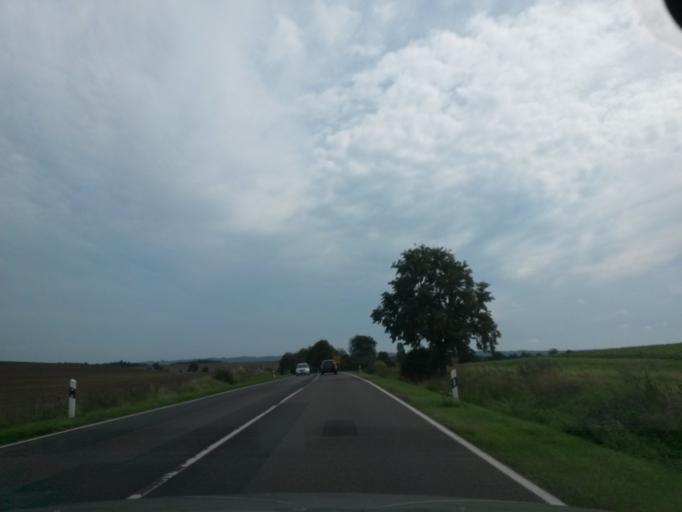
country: DE
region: Brandenburg
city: Meyenburg
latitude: 53.0270
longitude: 14.1976
